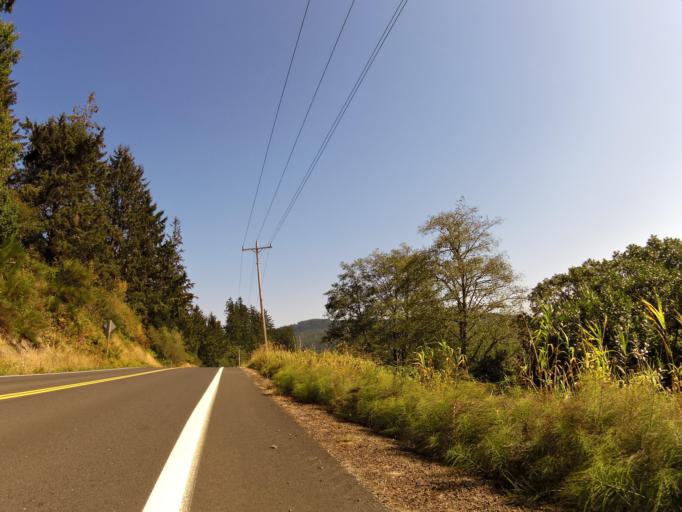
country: US
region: Oregon
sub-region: Tillamook County
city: Pacific City
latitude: 45.1807
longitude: -123.9386
